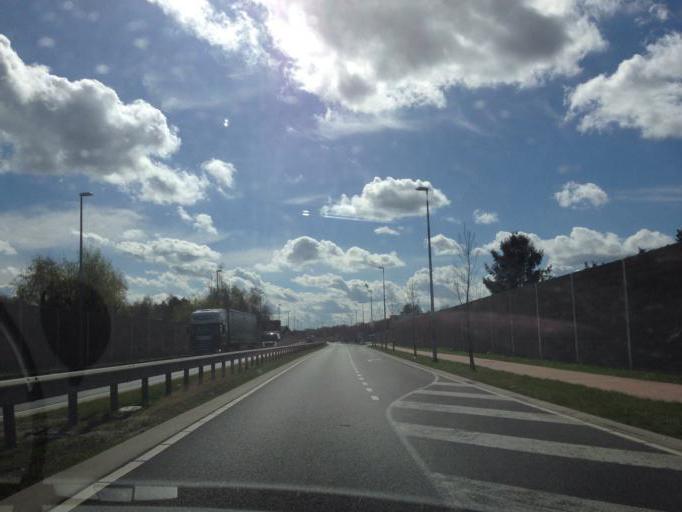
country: BE
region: Flanders
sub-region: Provincie Limburg
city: Genk
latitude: 50.9247
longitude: 5.4812
